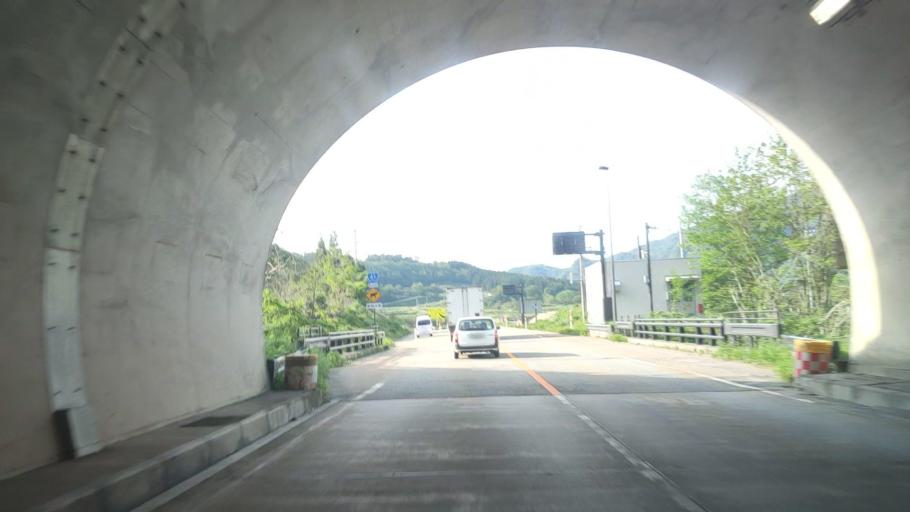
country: JP
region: Toyama
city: Yatsuomachi-higashikumisaka
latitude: 36.5314
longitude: 137.2261
